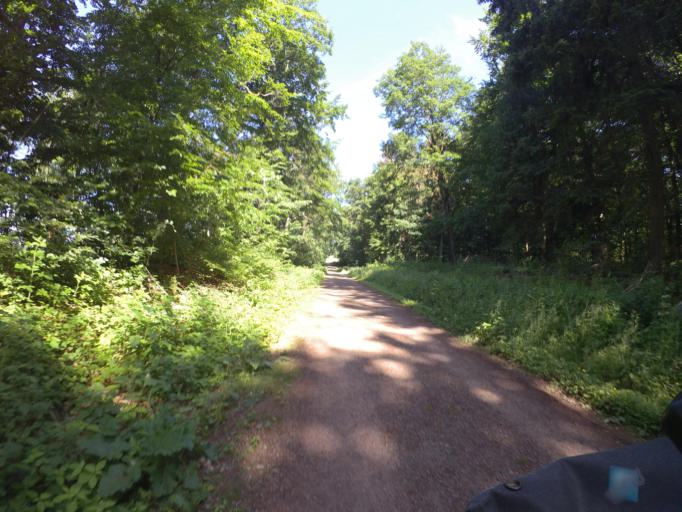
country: DE
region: Rheinland-Pfalz
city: Waldmohr
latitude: 49.3768
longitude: 7.2945
